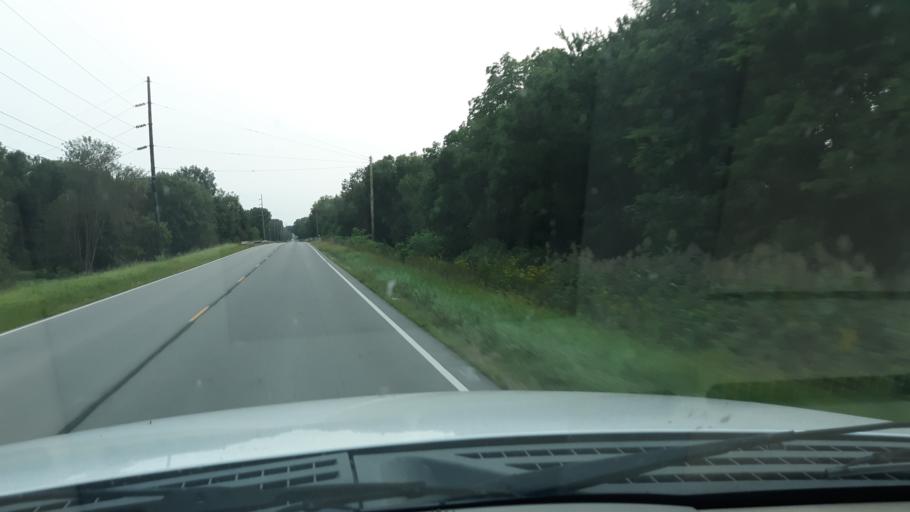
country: US
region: Illinois
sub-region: White County
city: Norris City
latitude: 37.9396
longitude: -88.3437
